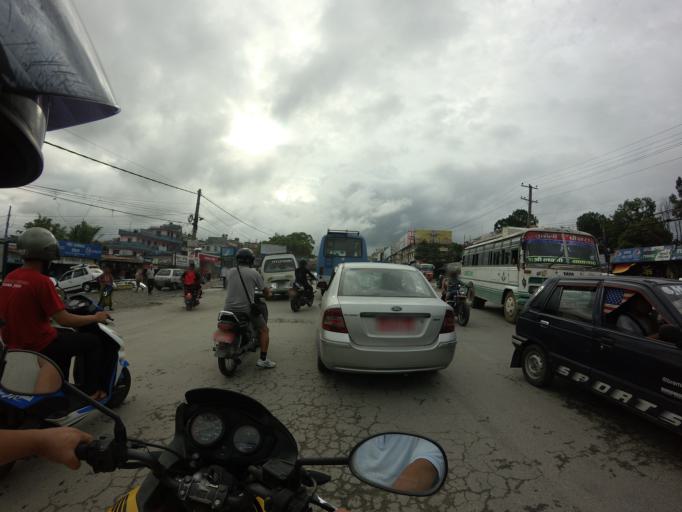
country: NP
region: Western Region
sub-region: Gandaki Zone
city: Pokhara
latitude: 28.2089
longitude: 83.9872
